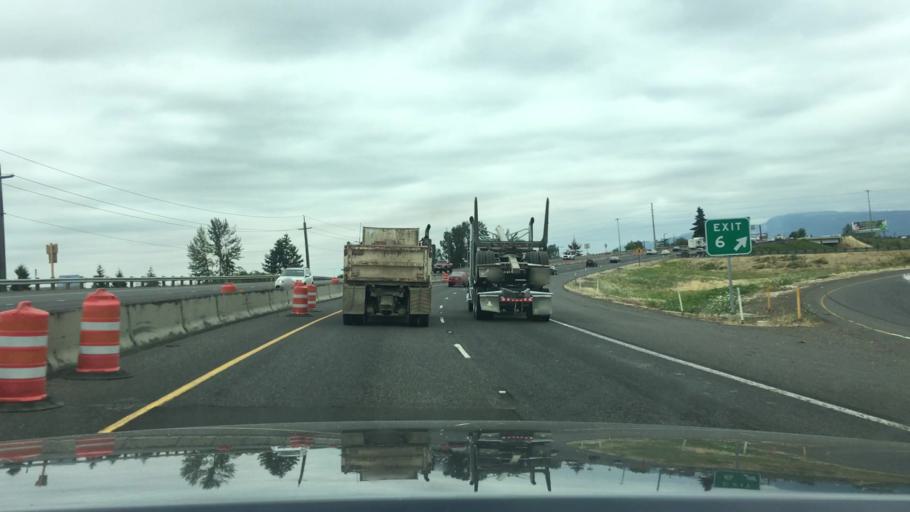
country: US
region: Oregon
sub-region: Lane County
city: Eugene
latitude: 44.0942
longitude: -123.1702
